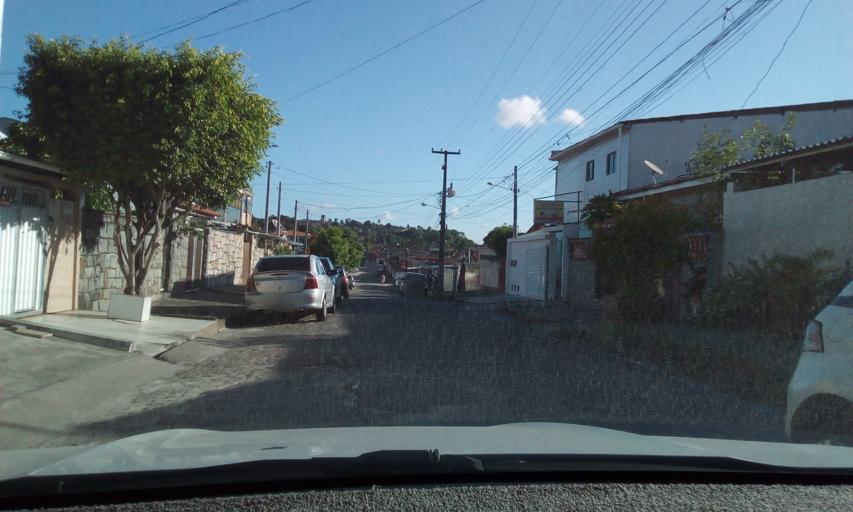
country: BR
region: Paraiba
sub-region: Bayeux
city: Bayeux
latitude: -7.1252
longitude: -34.9171
